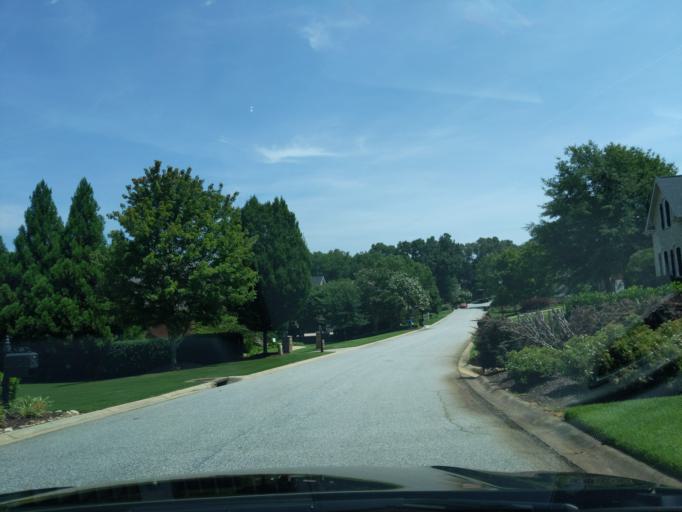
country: US
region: South Carolina
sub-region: Greenville County
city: Five Forks
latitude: 34.8363
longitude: -82.2154
